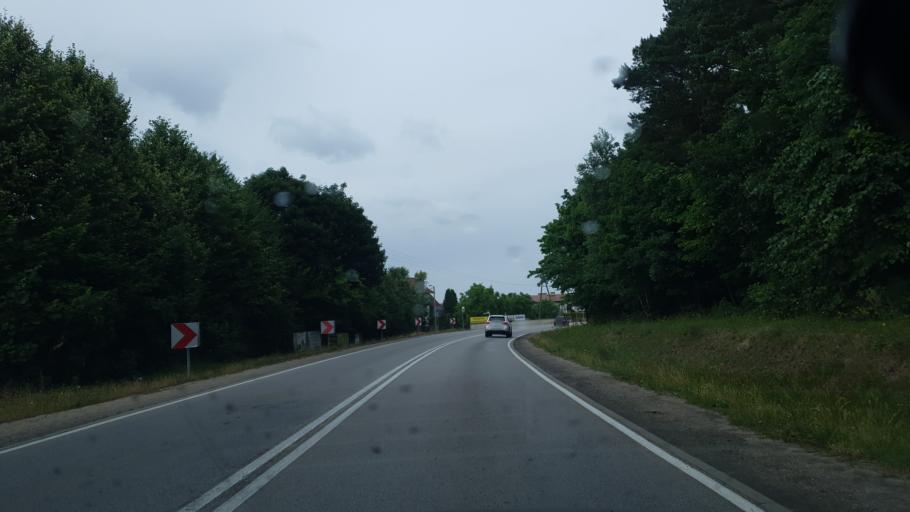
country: PL
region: Pomeranian Voivodeship
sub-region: Powiat kartuski
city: Banino
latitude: 54.4002
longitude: 18.3592
